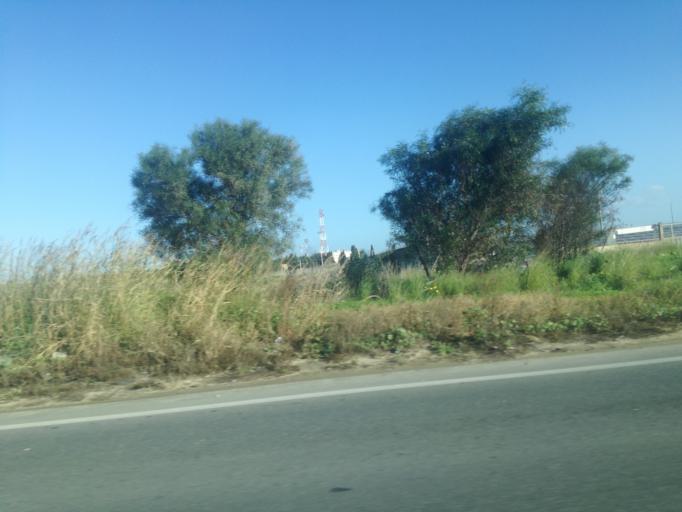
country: IT
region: Sicily
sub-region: Provincia di Caltanissetta
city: Gela
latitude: 37.0594
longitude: 14.2824
